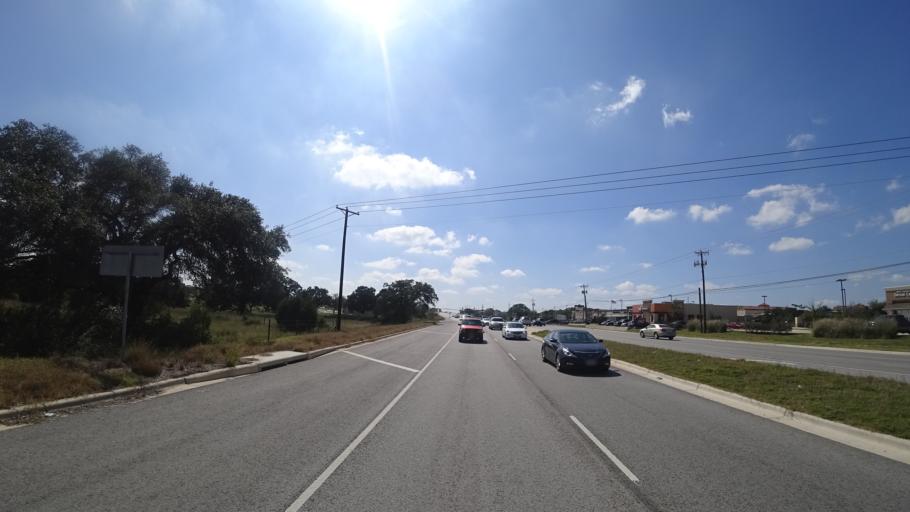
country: US
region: Texas
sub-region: Williamson County
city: Brushy Creek
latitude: 30.4972
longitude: -97.7230
